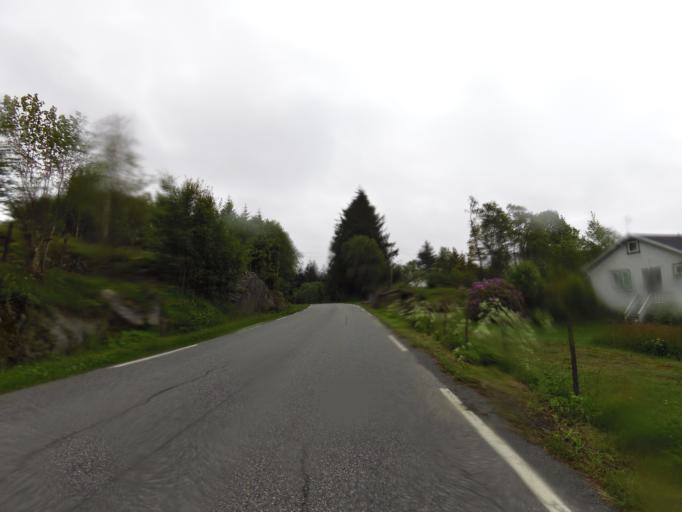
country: NO
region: Hordaland
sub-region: Sveio
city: Sveio
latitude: 59.5238
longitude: 5.2812
